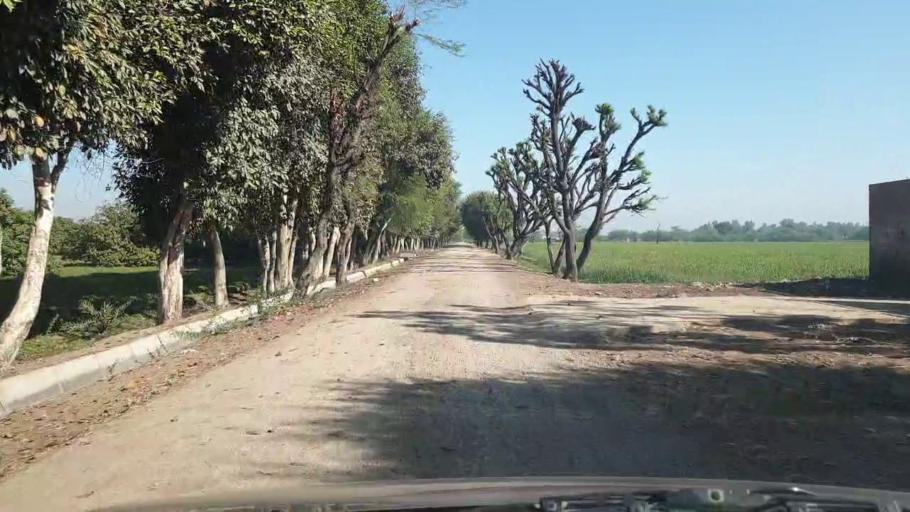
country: PK
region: Sindh
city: Umarkot
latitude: 25.3737
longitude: 69.7014
